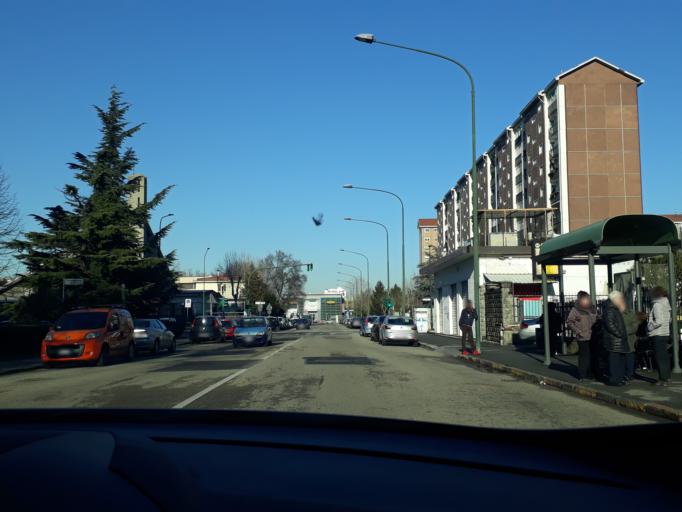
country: IT
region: Piedmont
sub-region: Provincia di Torino
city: Fornaci
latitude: 45.0190
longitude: 7.6114
